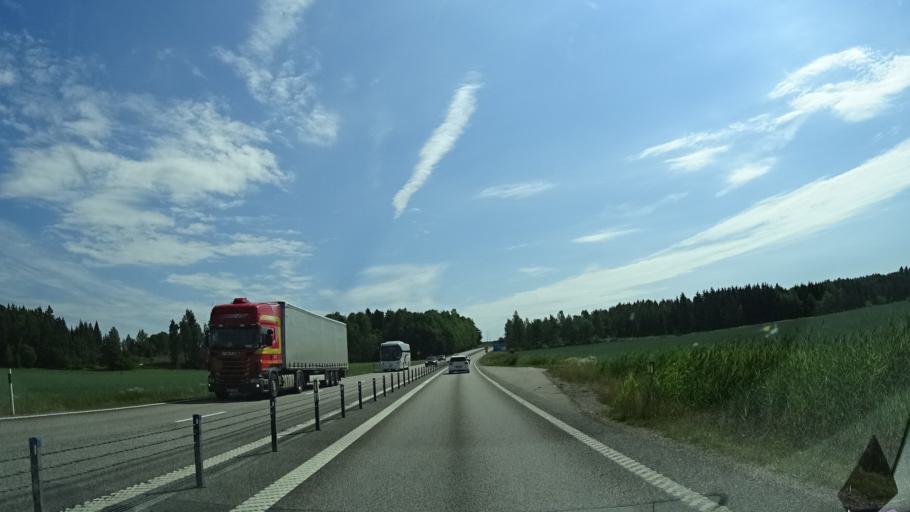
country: SE
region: Vaermland
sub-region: Kristinehamns Kommun
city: Kristinehamn
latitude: 59.3724
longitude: 14.0042
